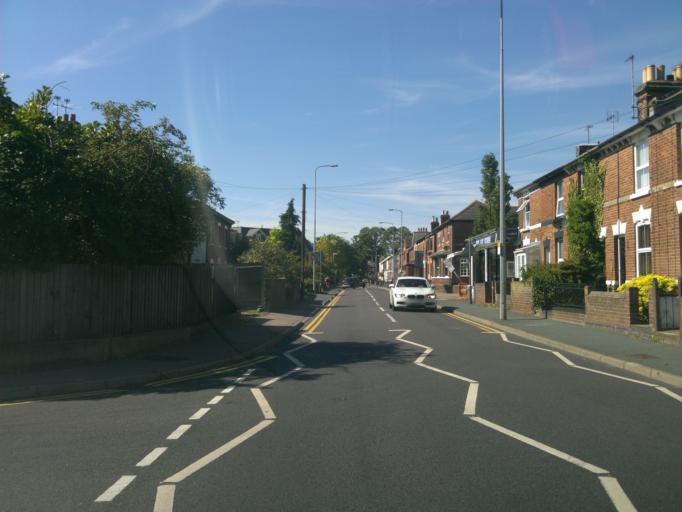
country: GB
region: England
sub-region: Essex
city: Colchester
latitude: 51.8788
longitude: 0.9065
